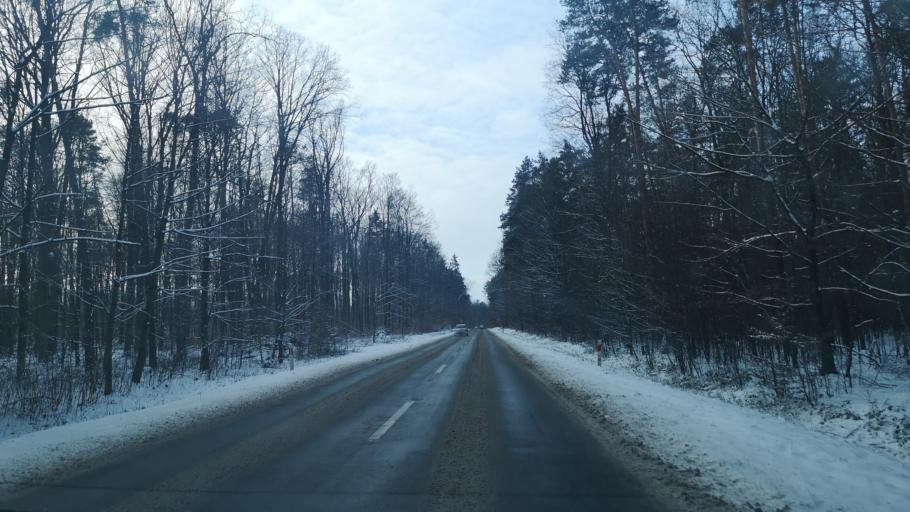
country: PL
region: Subcarpathian Voivodeship
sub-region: Powiat przeworski
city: Sieniawa
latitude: 50.2153
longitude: 22.6464
